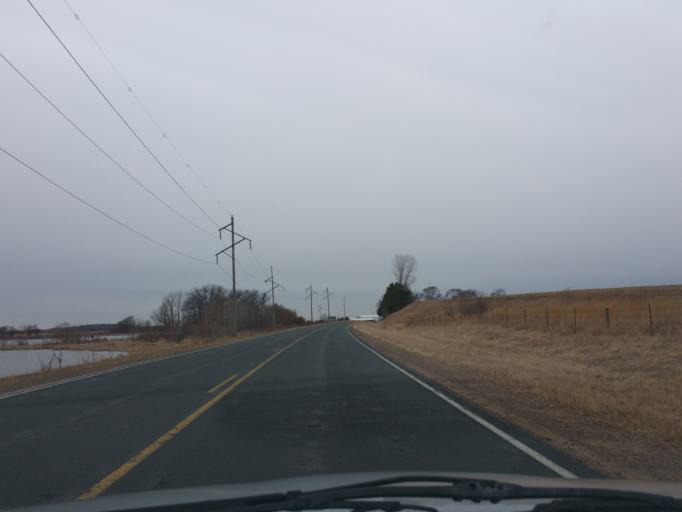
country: US
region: Wisconsin
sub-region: Saint Croix County
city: Roberts
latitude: 45.0359
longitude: -92.5869
